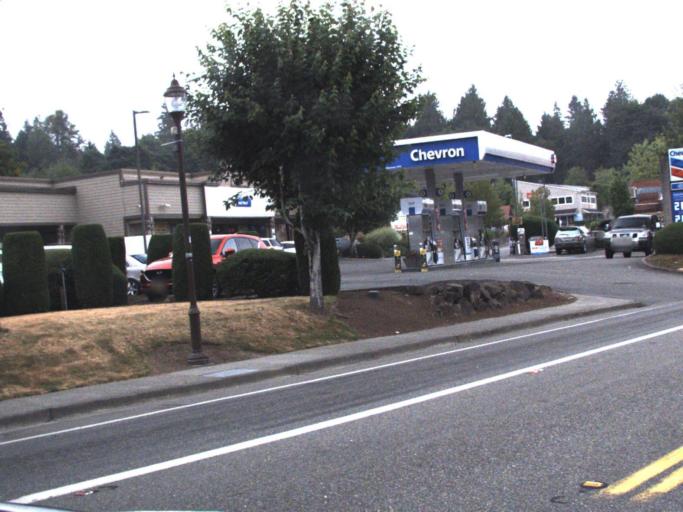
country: US
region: Washington
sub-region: King County
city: Duvall
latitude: 47.7398
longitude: -121.9863
